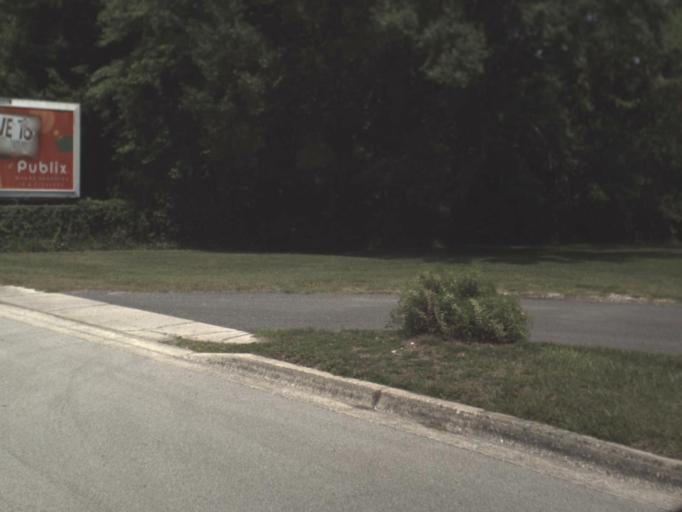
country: US
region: Florida
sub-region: Clay County
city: Bellair-Meadowbrook Terrace
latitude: 30.2889
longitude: -81.7945
